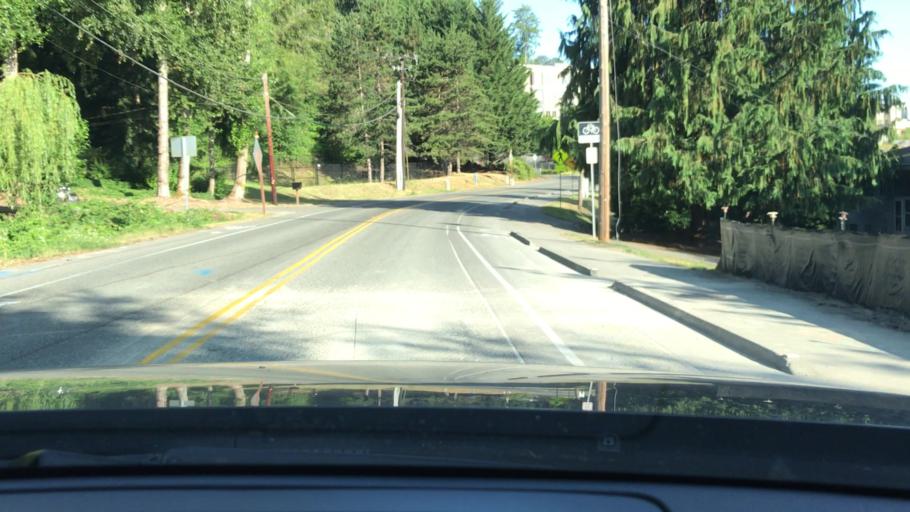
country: US
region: Washington
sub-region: King County
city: West Lake Sammamish
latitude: 47.5500
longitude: -122.0745
